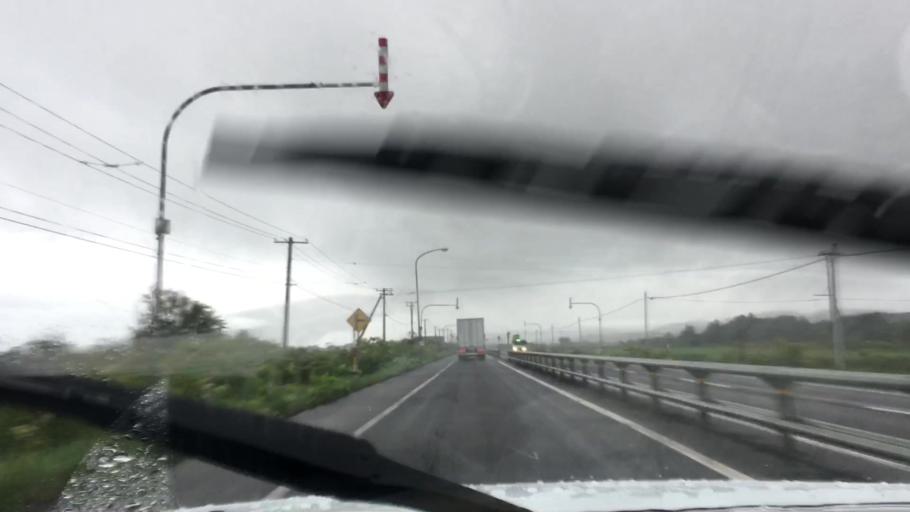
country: JP
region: Hokkaido
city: Niseko Town
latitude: 42.4176
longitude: 140.3108
